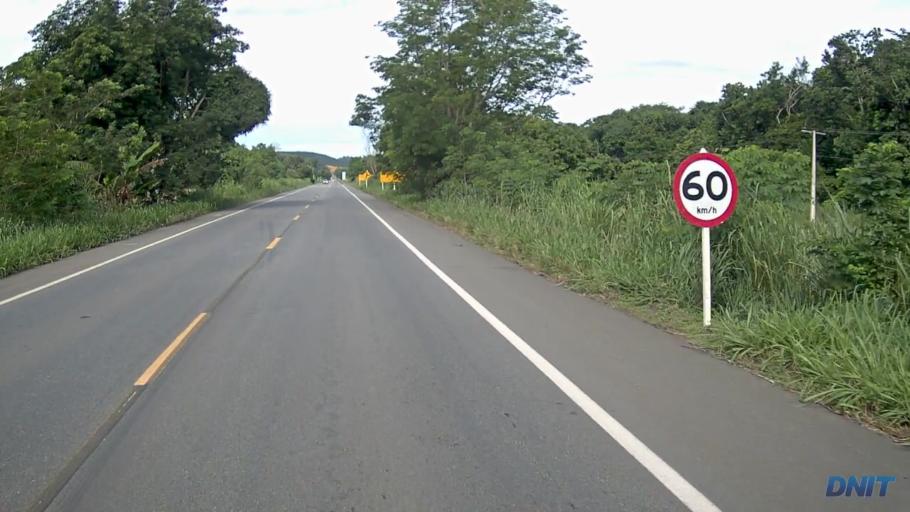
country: BR
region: Minas Gerais
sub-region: Ipaba
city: Ipaba
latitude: -19.2999
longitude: -42.3756
